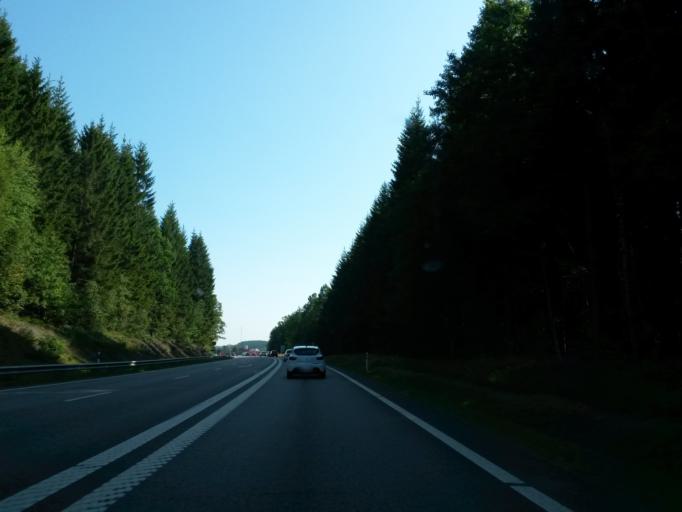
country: SE
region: Vaestra Goetaland
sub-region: Vargarda Kommun
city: Vargarda
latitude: 58.0476
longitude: 12.8109
